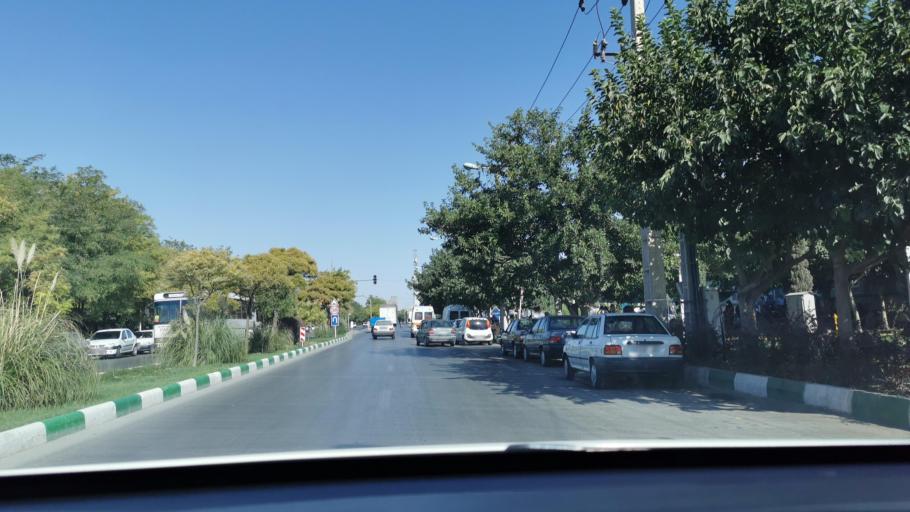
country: IR
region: Razavi Khorasan
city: Mashhad
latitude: 36.3323
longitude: 59.6386
